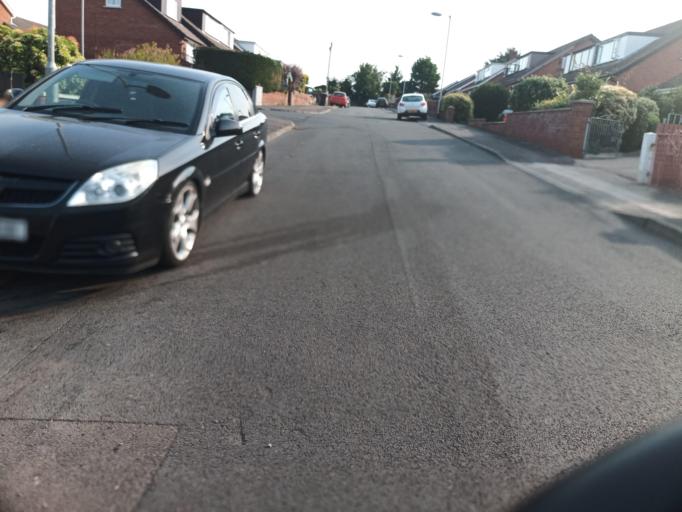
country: GB
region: Northern Ireland
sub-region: Ards District
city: Comber
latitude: 54.5571
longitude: -5.7324
